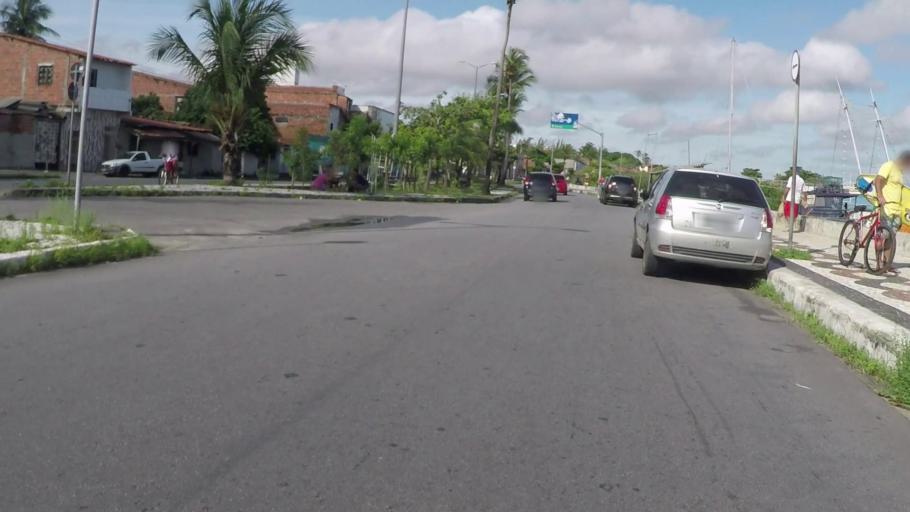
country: BR
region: Ceara
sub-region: Fortaleza
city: Fortaleza
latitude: -3.7007
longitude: -38.5889
